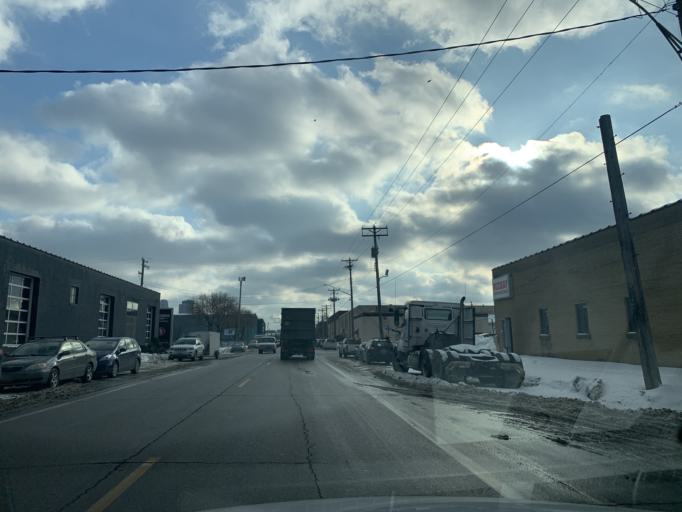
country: US
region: Minnesota
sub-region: Hennepin County
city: Minneapolis
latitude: 45.0043
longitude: -93.2802
